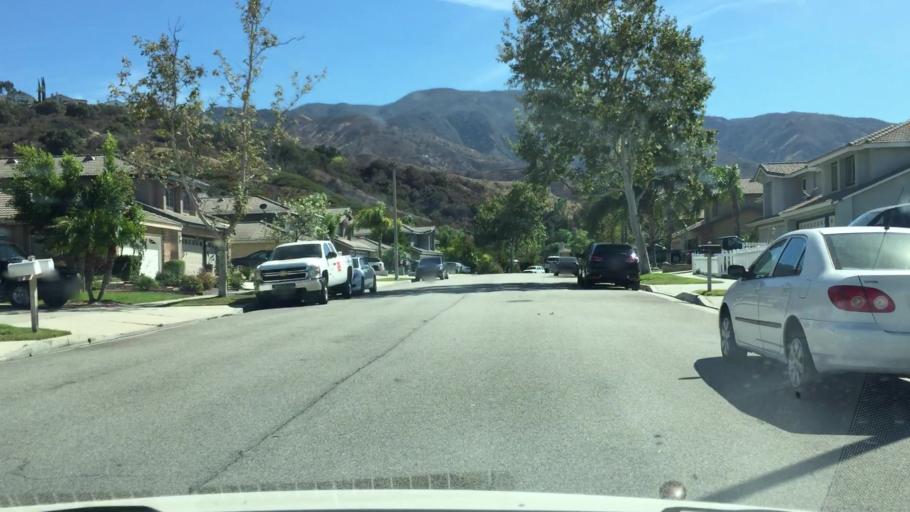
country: US
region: California
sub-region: Riverside County
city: Corona
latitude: 33.8719
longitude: -117.6272
